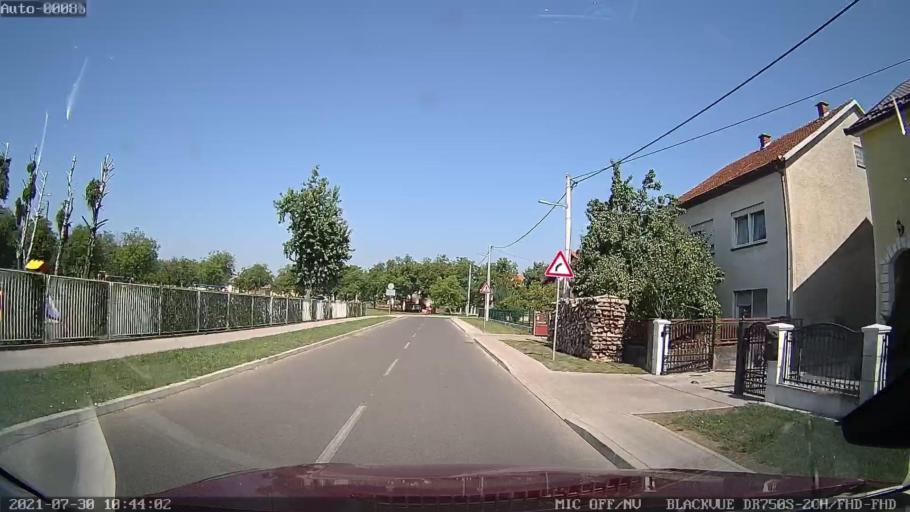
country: HR
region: Medimurska
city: Kursanec
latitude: 46.2944
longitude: 16.4067
